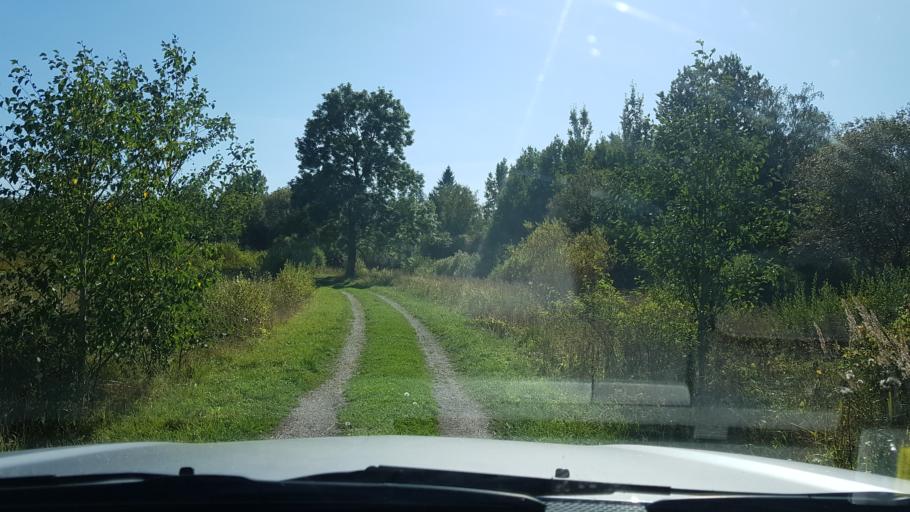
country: EE
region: Ida-Virumaa
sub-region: Sillamaee linn
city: Sillamae
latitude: 59.3834
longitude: 27.8737
